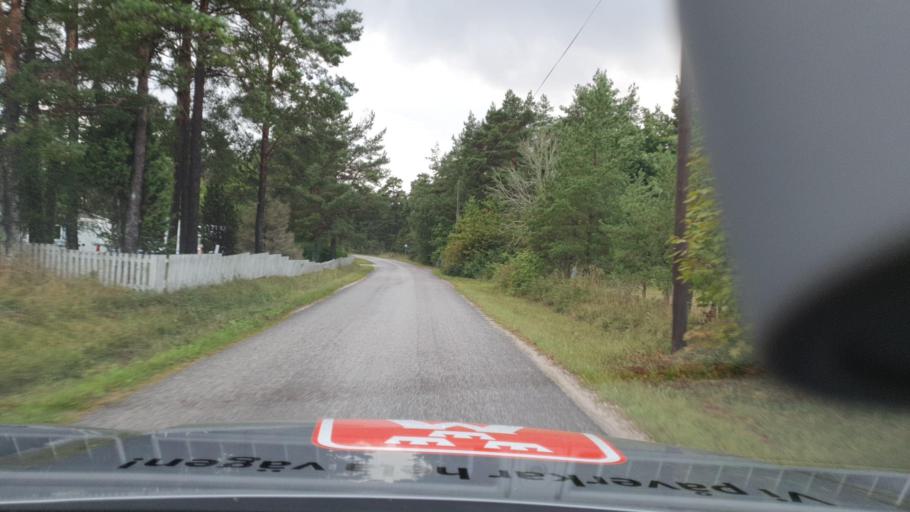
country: SE
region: Gotland
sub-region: Gotland
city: Vibble
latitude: 57.5461
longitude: 18.2302
